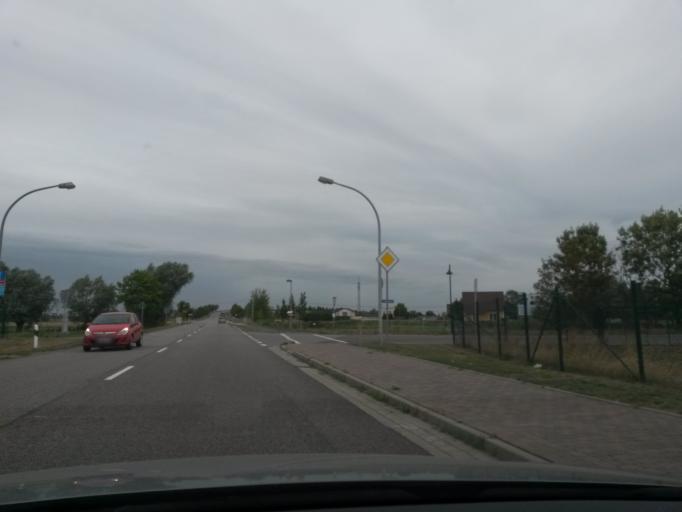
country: DE
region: Saxony-Anhalt
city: Schonhausen
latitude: 52.5863
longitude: 12.0359
